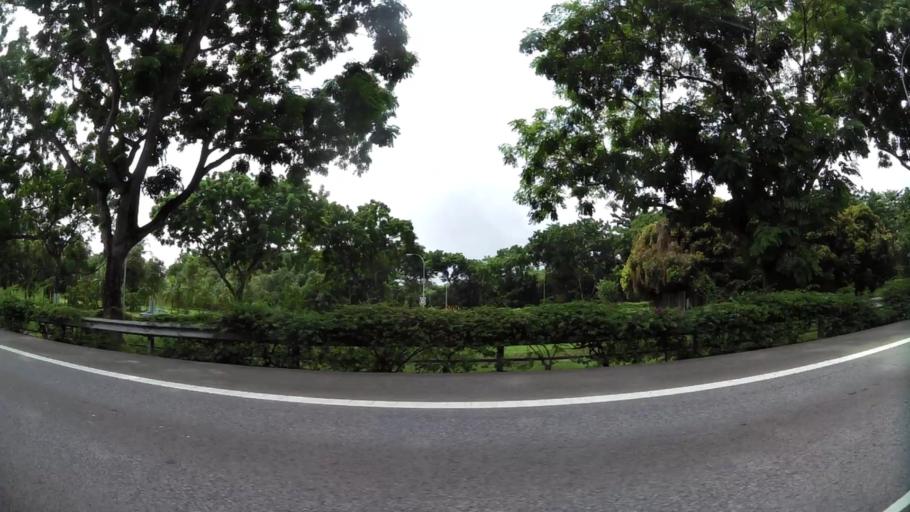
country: SG
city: Singapore
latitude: 1.3676
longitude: 103.9451
